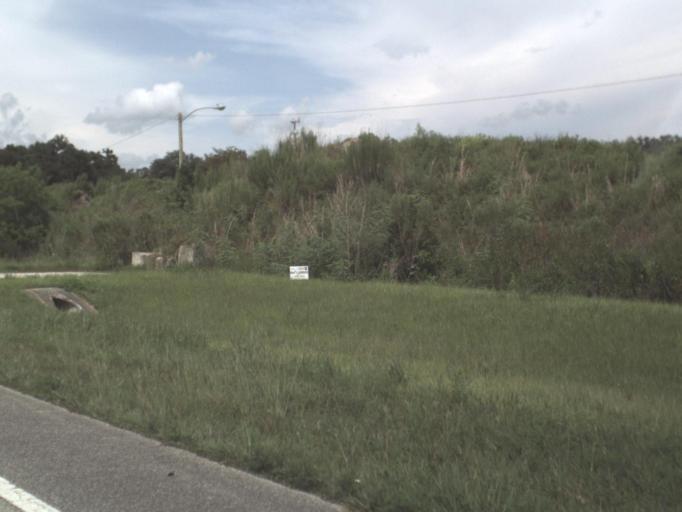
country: US
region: Florida
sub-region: Hernando County
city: South Brooksville
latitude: 28.5031
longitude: -82.4234
